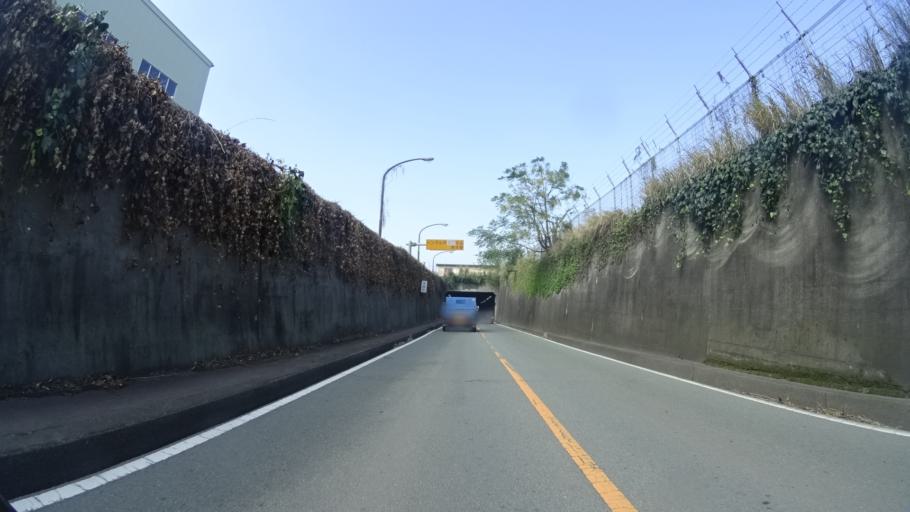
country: JP
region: Kumamoto
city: Ozu
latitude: 32.8341
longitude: 130.8556
